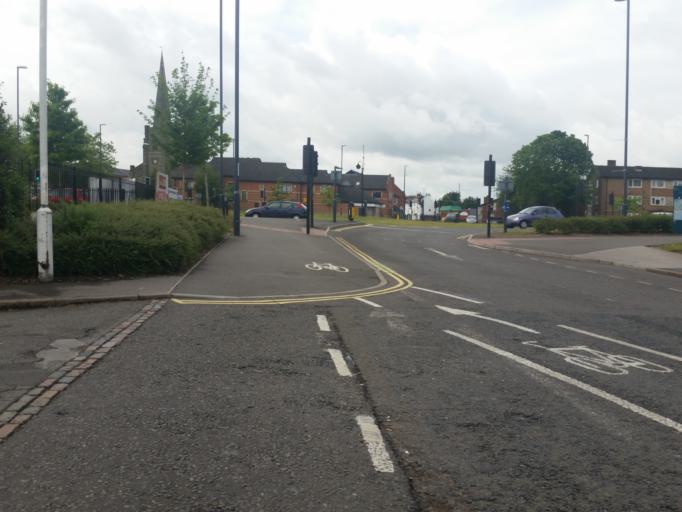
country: GB
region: England
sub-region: Derby
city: Derby
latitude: 52.9181
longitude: -1.4776
